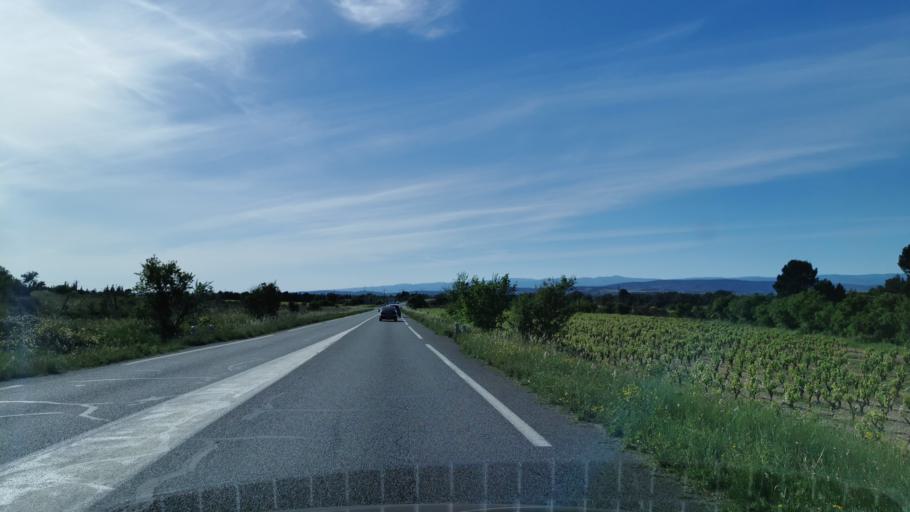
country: FR
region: Languedoc-Roussillon
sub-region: Departement de l'Aude
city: Nevian
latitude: 43.2075
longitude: 2.8825
